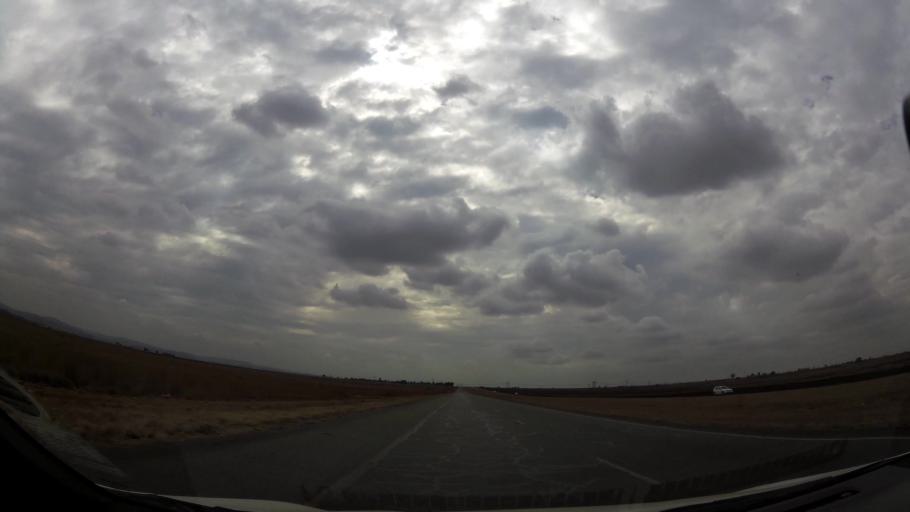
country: ZA
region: Gauteng
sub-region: Ekurhuleni Metropolitan Municipality
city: Germiston
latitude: -26.3723
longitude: 28.0913
